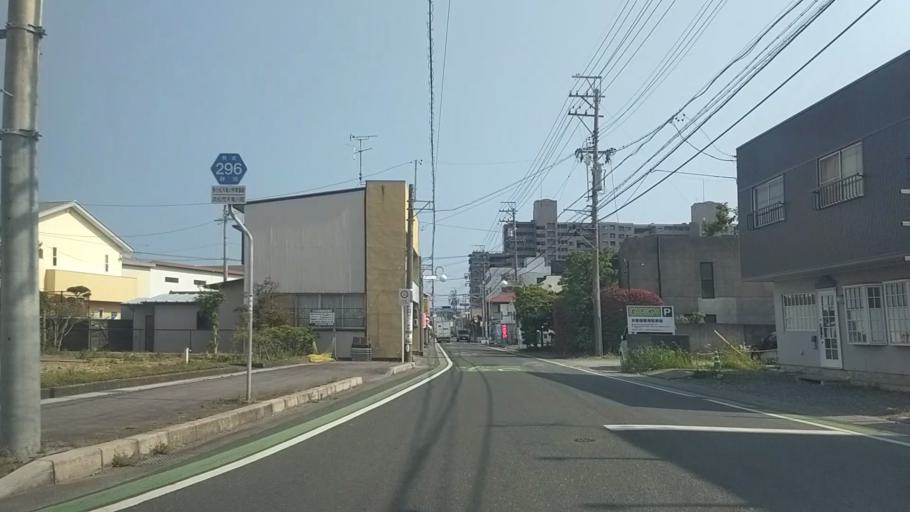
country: JP
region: Shizuoka
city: Hamamatsu
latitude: 34.7206
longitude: 137.7779
